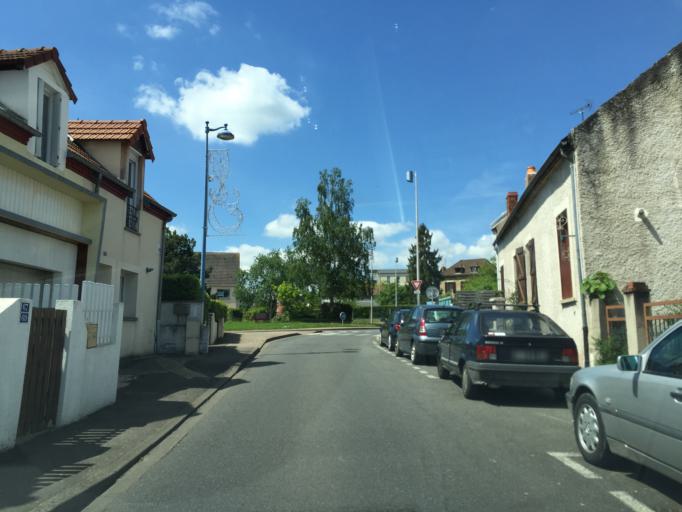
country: FR
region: Auvergne
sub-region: Departement de l'Allier
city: Bellerive-sur-Allier
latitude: 46.1171
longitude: 3.4047
